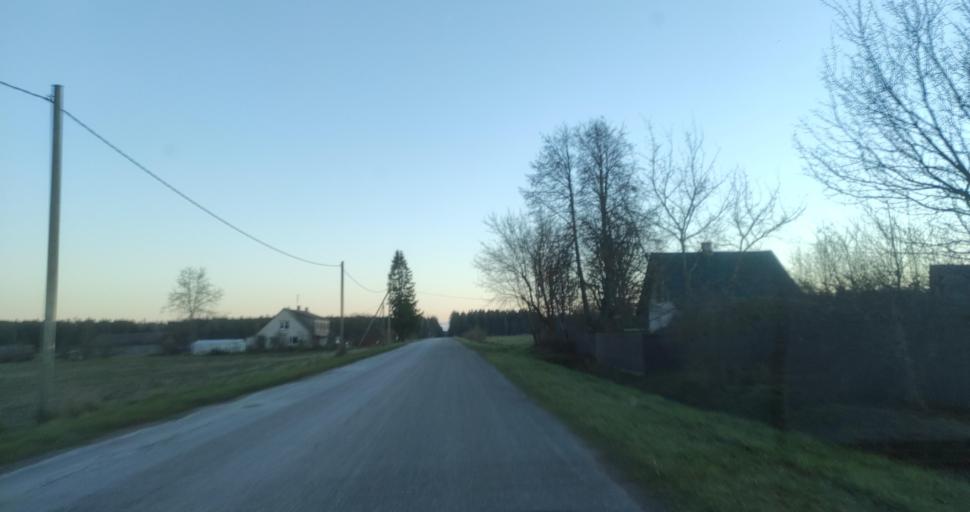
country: LV
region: Dundaga
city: Dundaga
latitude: 57.3739
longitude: 22.2311
